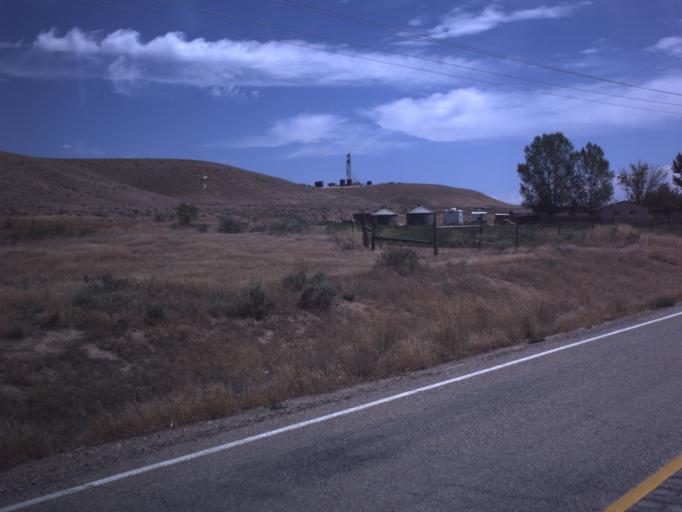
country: US
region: Utah
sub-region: Uintah County
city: Naples
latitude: 40.2144
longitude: -109.6742
